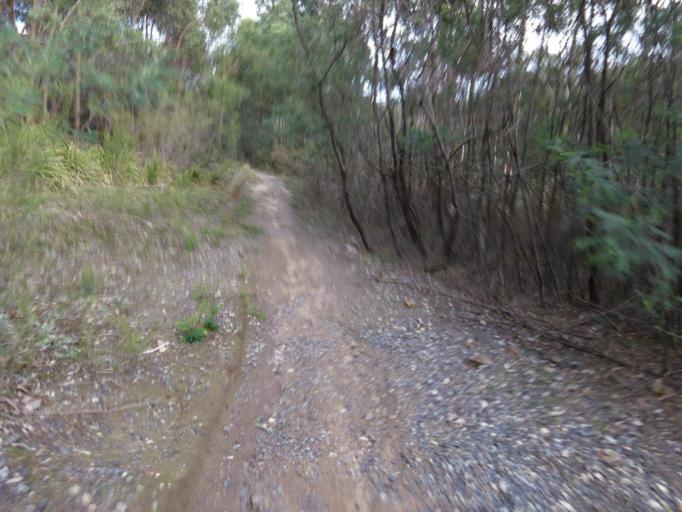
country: AU
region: Victoria
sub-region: Yarra Ranges
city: Lysterfield
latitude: -37.9443
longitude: 145.2763
